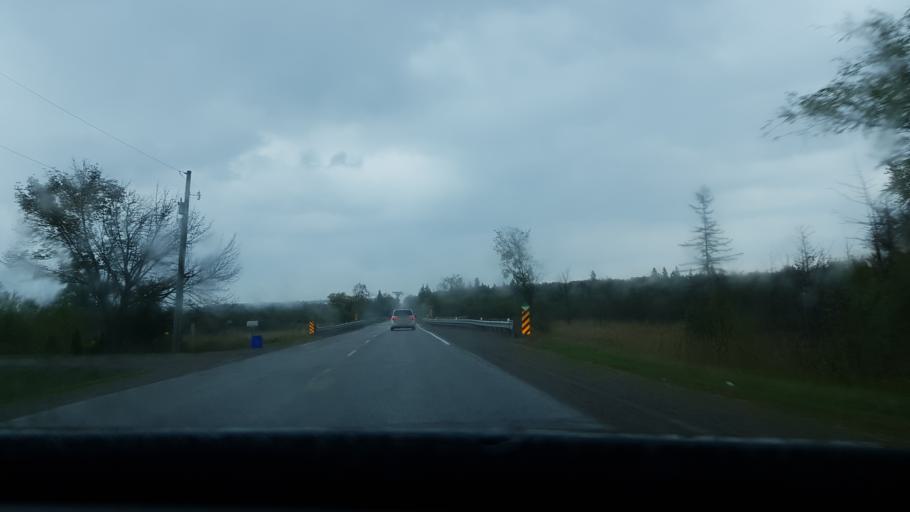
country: CA
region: Ontario
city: Omemee
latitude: 44.3905
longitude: -78.5736
